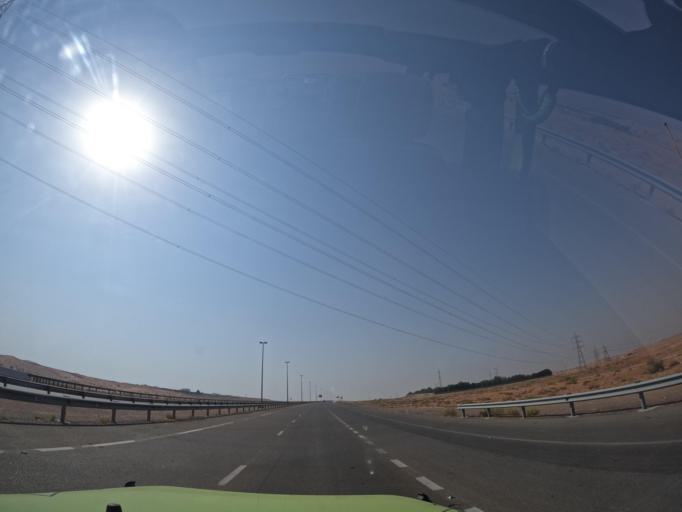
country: OM
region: Al Buraimi
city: Al Buraymi
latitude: 24.3844
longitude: 55.7263
